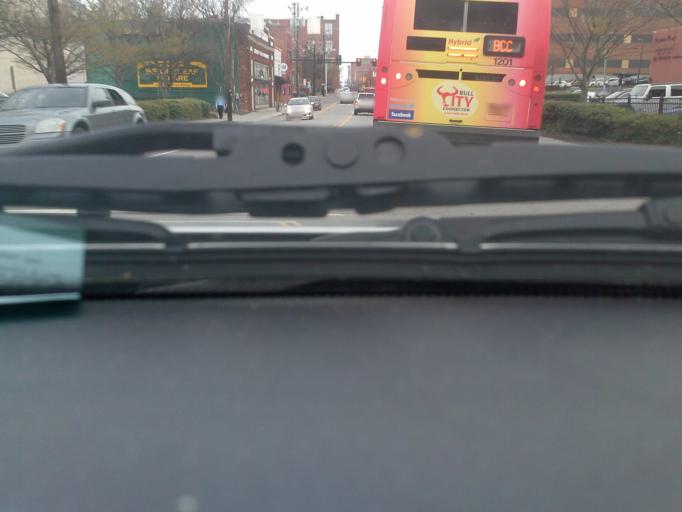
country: US
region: North Carolina
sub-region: Durham County
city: Durham
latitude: 36.0000
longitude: -78.9093
